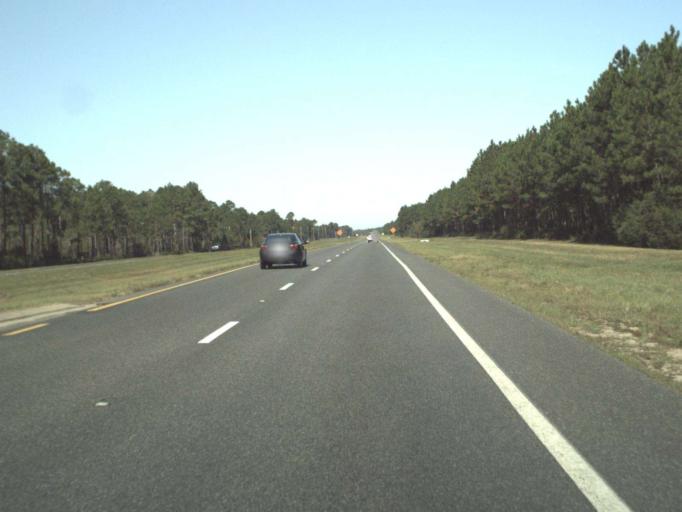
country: US
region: Florida
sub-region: Walton County
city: Seaside
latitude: 30.3336
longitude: -86.0589
